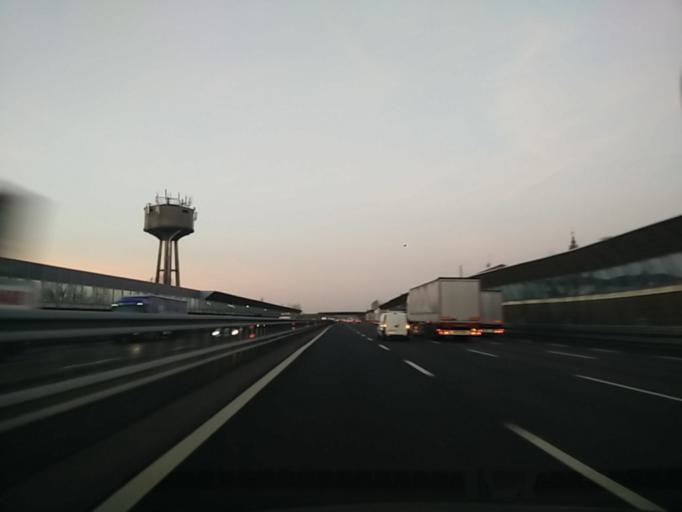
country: IT
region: Lombardy
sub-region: Provincia di Bergamo
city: Osio Sopra
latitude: 45.6308
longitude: 9.5963
